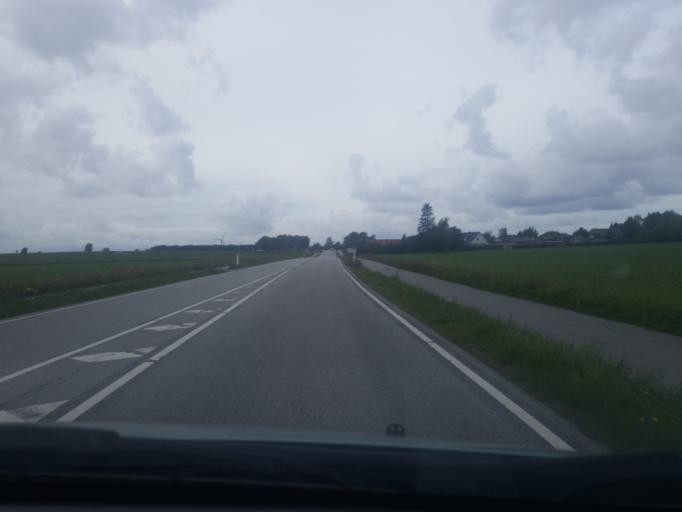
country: DK
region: Zealand
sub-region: Guldborgsund Kommune
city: Nykobing Falster
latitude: 54.7041
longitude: 11.9246
